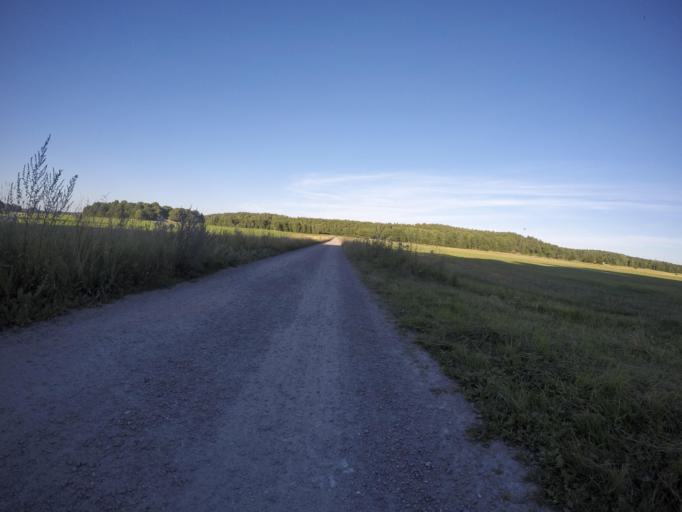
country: SE
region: Vaestmanland
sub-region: Vasteras
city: Vasteras
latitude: 59.5705
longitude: 16.6425
